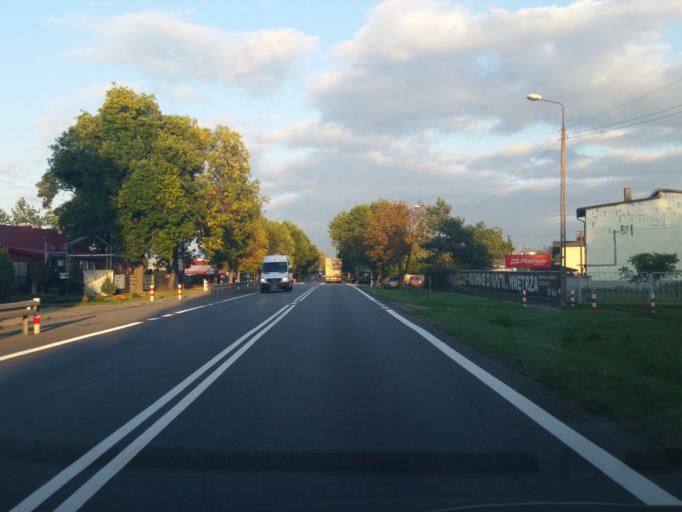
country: PL
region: Masovian Voivodeship
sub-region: Powiat warszawski zachodni
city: Jozefow
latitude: 52.2128
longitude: 20.6978
